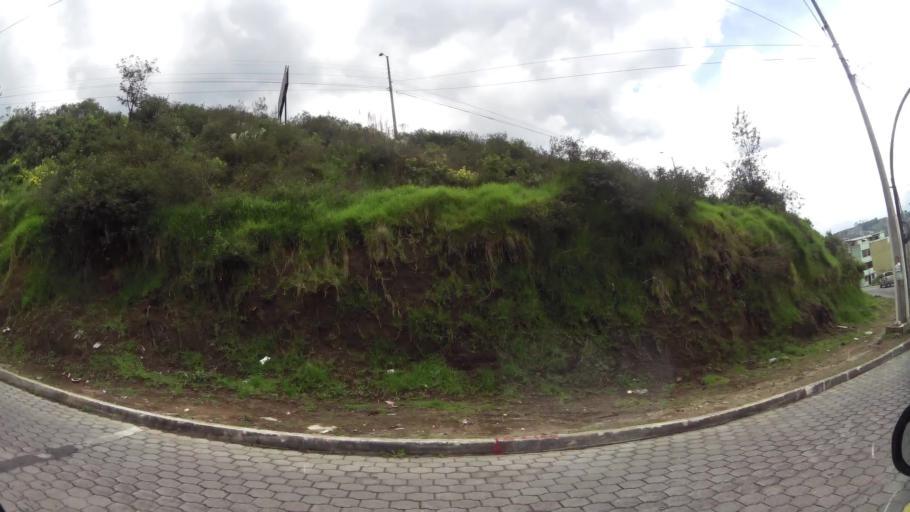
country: EC
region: Pichincha
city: Quito
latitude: -0.2429
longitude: -78.4961
